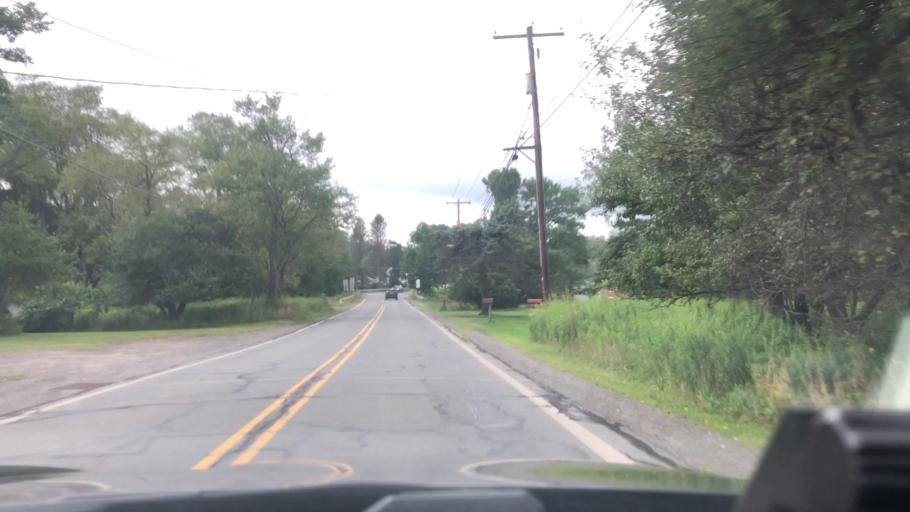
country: US
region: Pennsylvania
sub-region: Lackawanna County
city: Moscow
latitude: 41.2451
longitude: -75.4826
